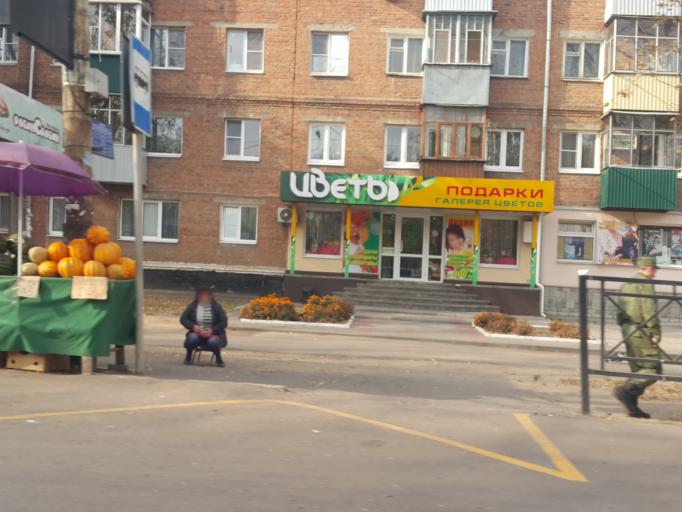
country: RU
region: Tambov
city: Pokrovo-Prigorodnoye
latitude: 52.6831
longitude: 41.4624
